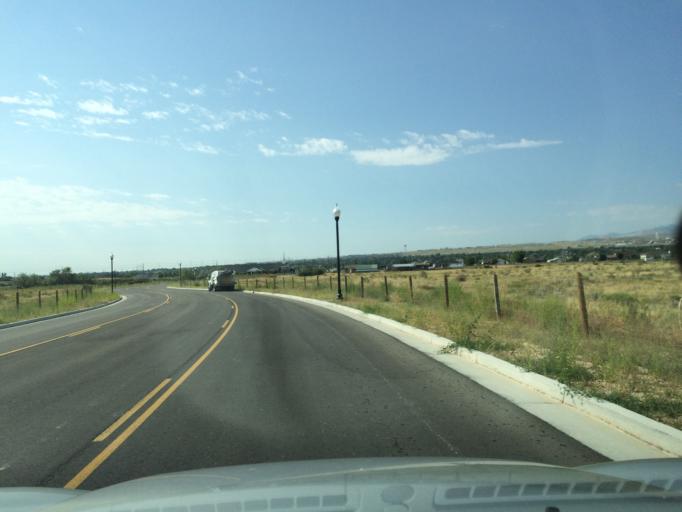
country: US
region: Utah
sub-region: Salt Lake County
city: West Valley City
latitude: 40.7140
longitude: -112.0451
